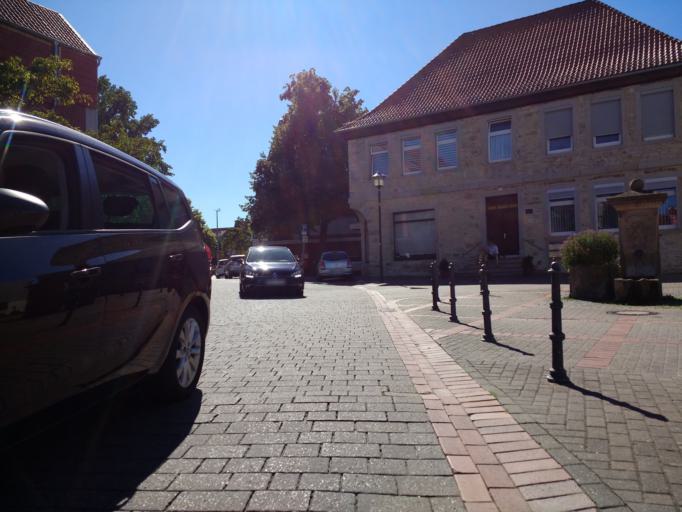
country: DE
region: Lower Saxony
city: Weyhausen
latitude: 52.4188
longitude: 10.7168
